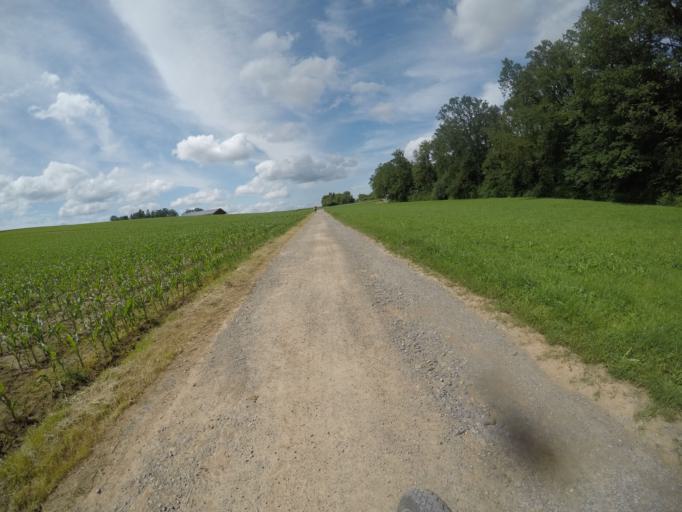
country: DE
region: Baden-Wuerttemberg
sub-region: Regierungsbezirk Stuttgart
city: Steinenbronn
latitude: 48.6973
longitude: 9.1288
